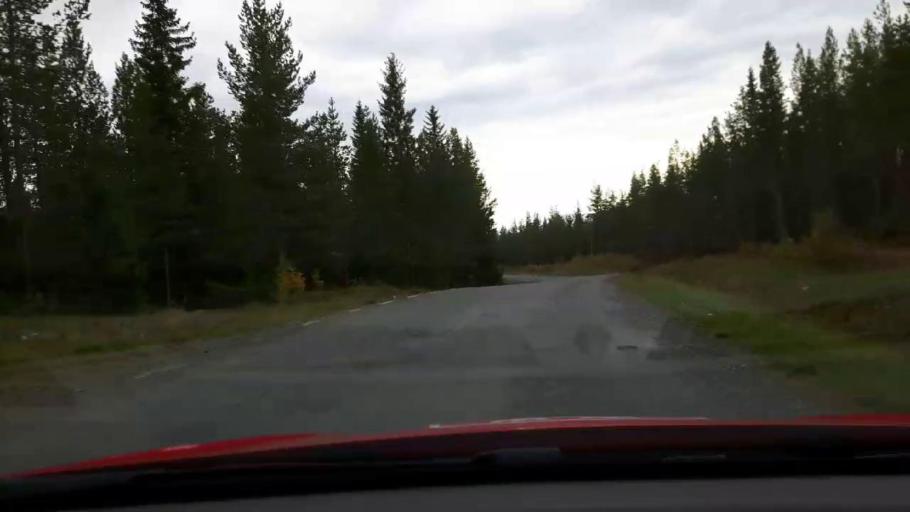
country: SE
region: Jaemtland
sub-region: Krokoms Kommun
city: Krokom
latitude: 63.2142
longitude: 14.1185
